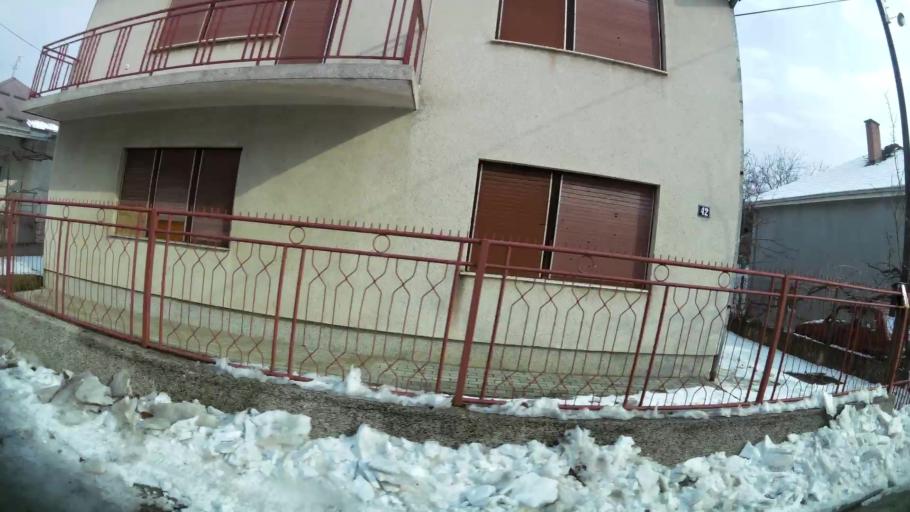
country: MK
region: Saraj
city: Saraj
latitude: 42.0193
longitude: 21.3569
